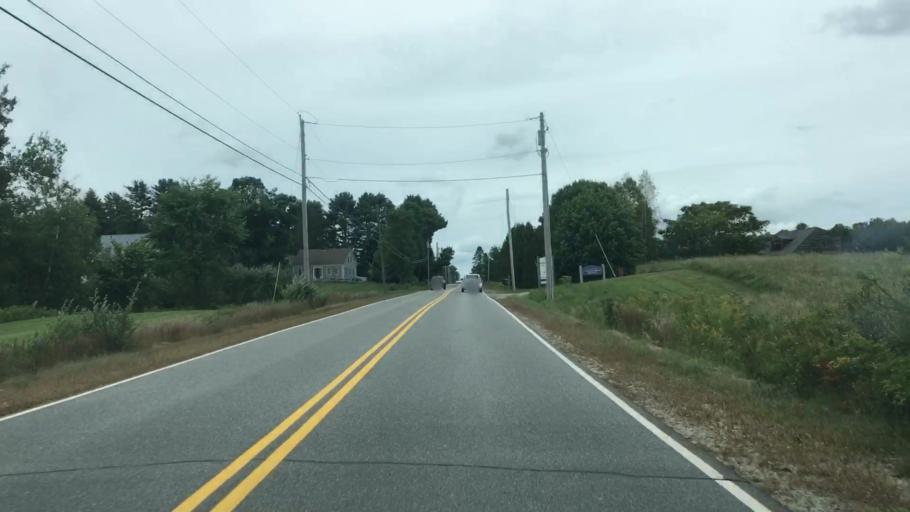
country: US
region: Maine
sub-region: Cumberland County
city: Yarmouth
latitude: 43.8642
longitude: -70.2241
